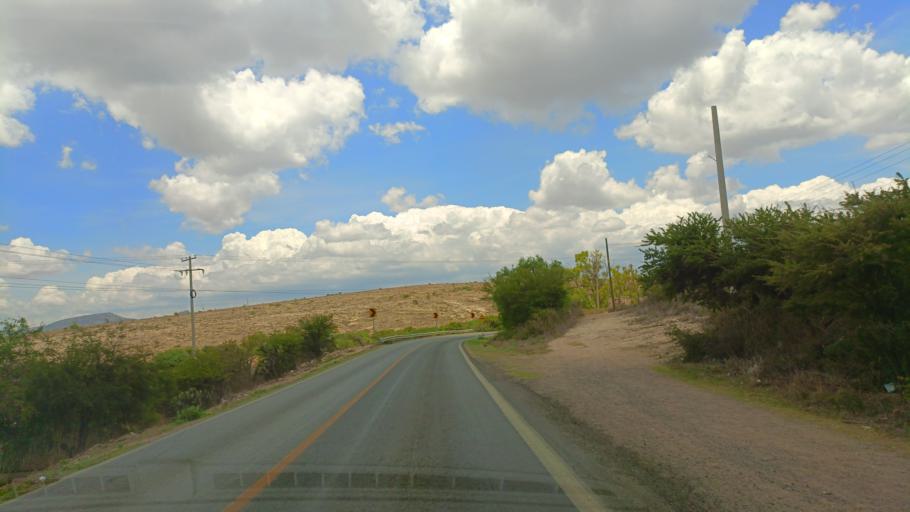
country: MX
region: Guanajuato
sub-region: San Luis de la Paz
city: San Ignacio
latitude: 21.2332
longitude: -100.4901
